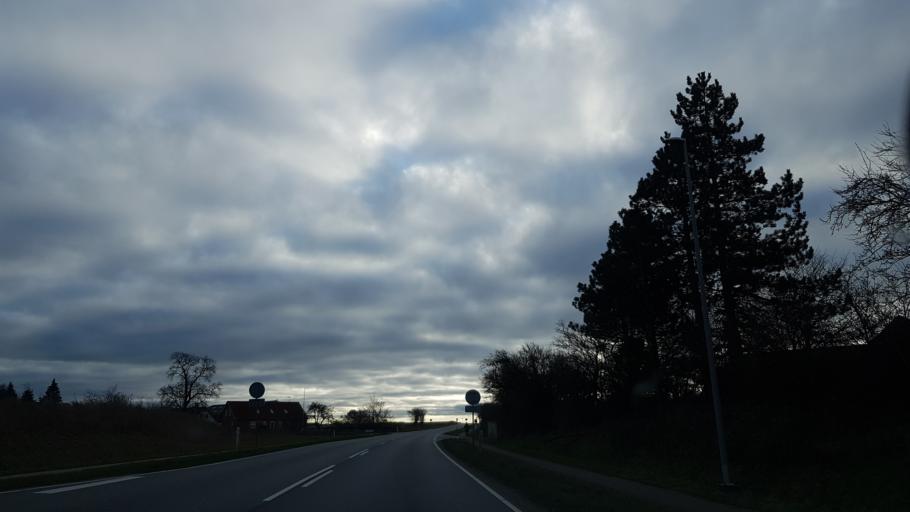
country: DK
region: Zealand
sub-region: Kalundborg Kommune
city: Hong
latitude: 55.4866
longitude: 11.2970
